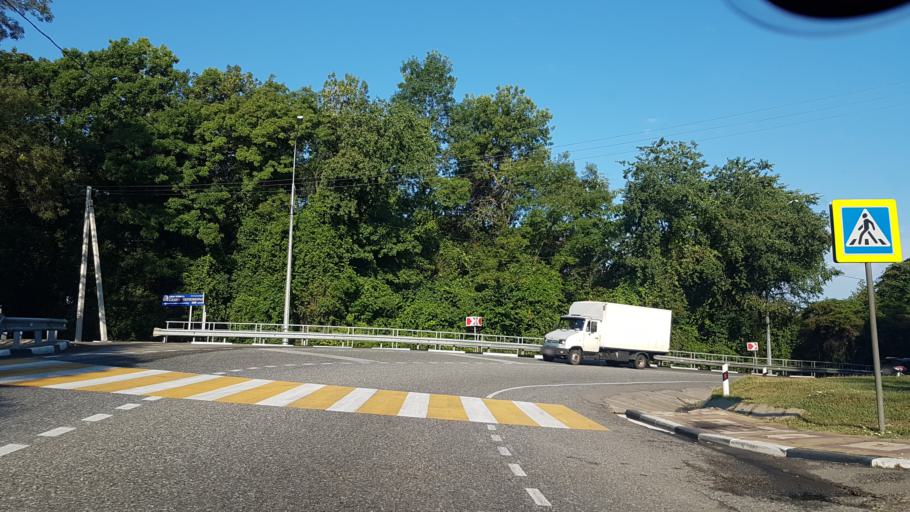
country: RU
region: Krasnodarskiy
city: Vardane
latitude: 43.7534
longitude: 39.5244
